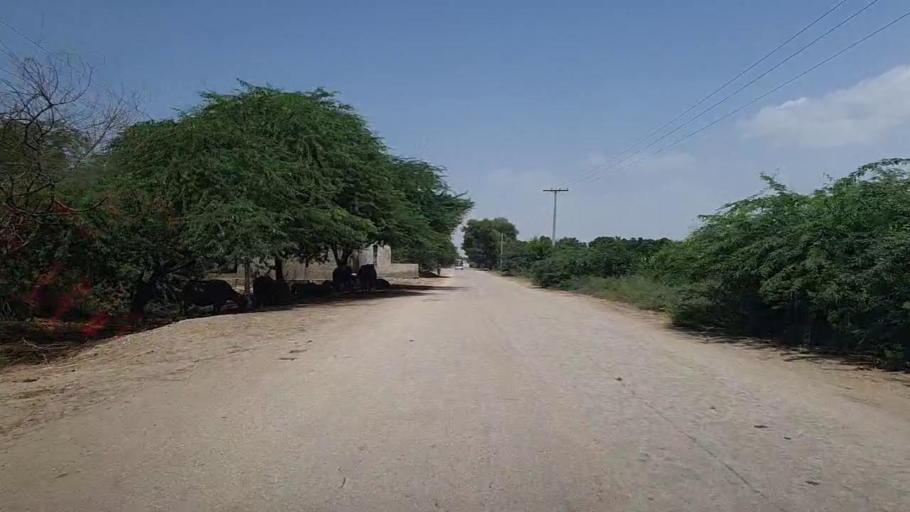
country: PK
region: Sindh
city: Pad Idan
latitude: 26.7832
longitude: 68.3313
